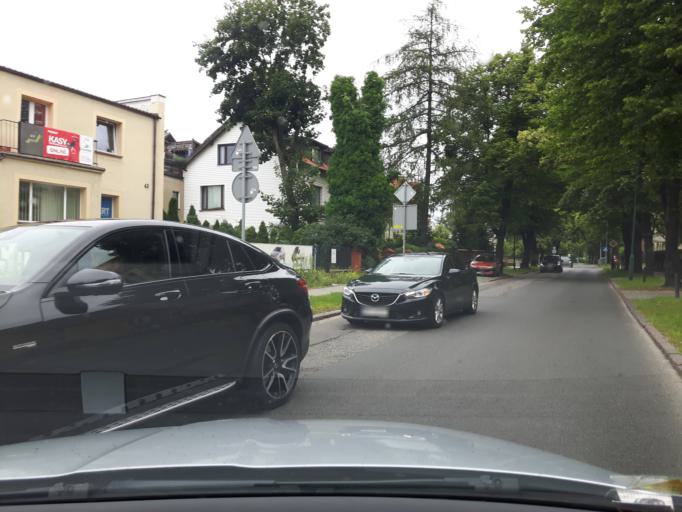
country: PL
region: Pomeranian Voivodeship
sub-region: Sopot
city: Sopot
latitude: 54.4132
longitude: 18.5762
